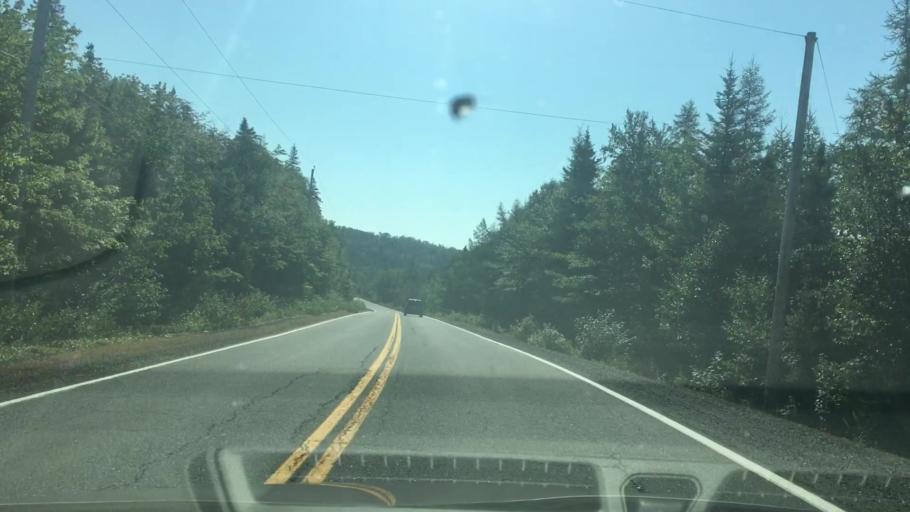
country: CA
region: Nova Scotia
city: Cole Harbour
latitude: 44.8079
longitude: -62.8337
